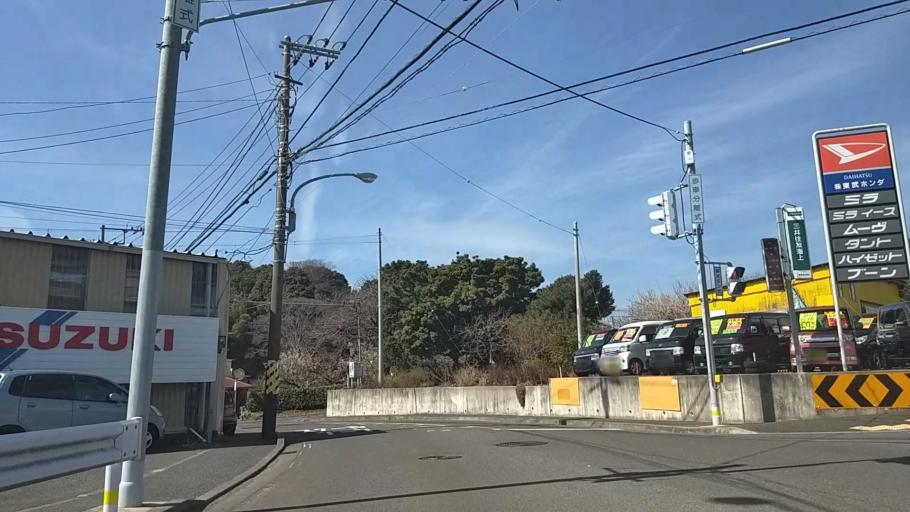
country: JP
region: Kanagawa
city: Fujisawa
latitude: 35.3905
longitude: 139.5105
